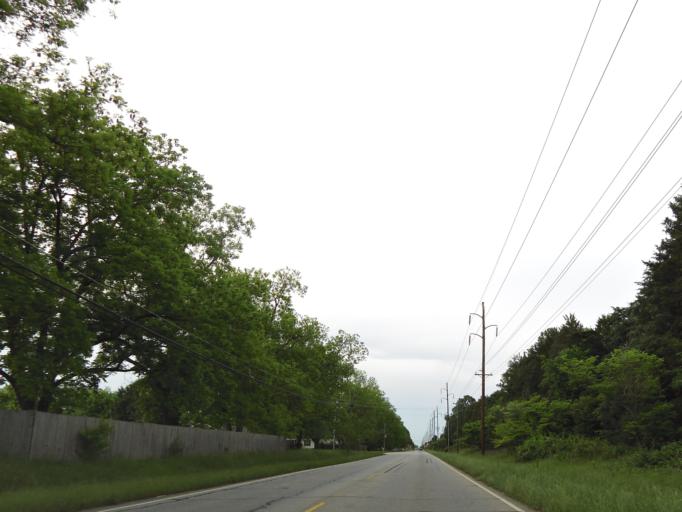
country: US
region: Georgia
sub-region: Houston County
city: Centerville
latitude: 32.6472
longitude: -83.7088
